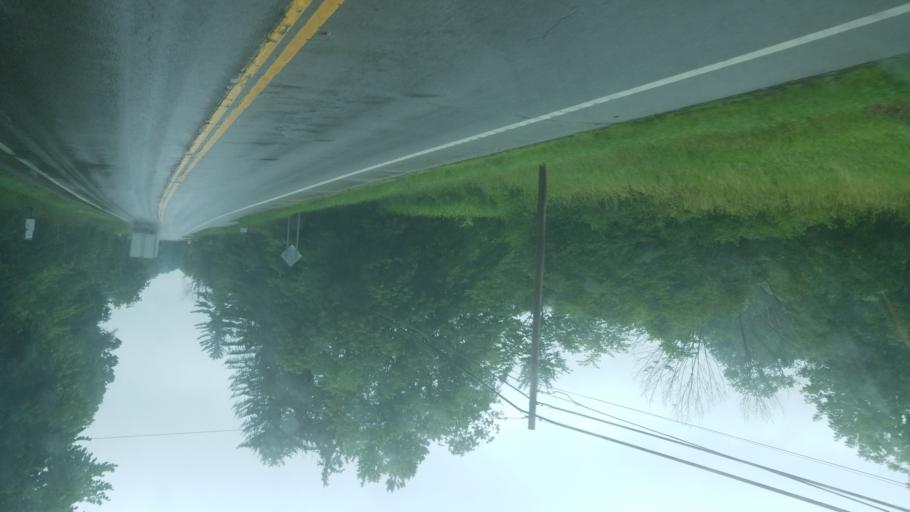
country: US
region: Ohio
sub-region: Richland County
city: Lexington
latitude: 40.7060
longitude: -82.5544
